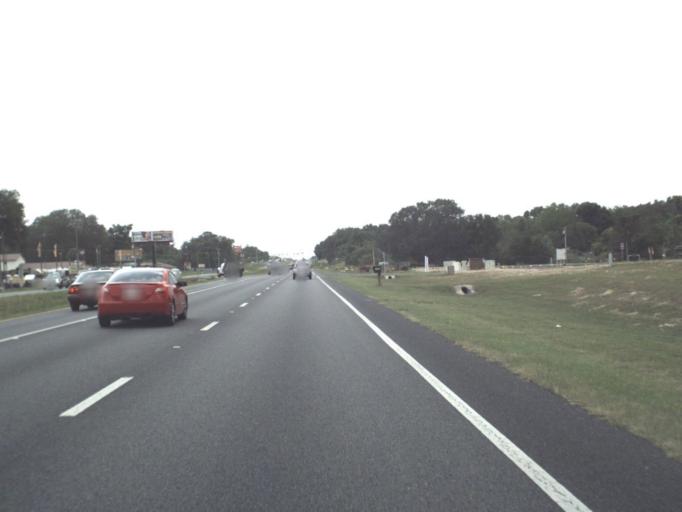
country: US
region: Florida
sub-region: Marion County
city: Belleview
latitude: 29.0135
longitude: -82.0106
